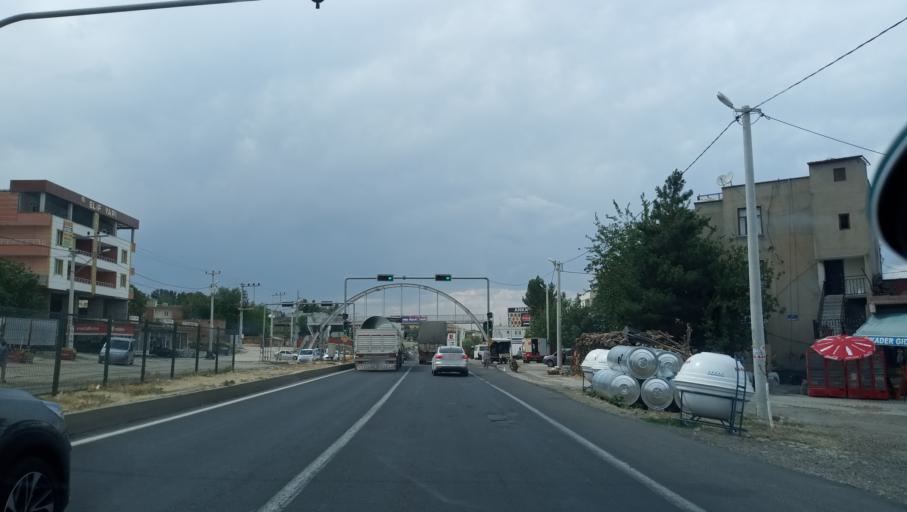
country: TR
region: Diyarbakir
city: Sur
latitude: 37.8413
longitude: 40.2300
